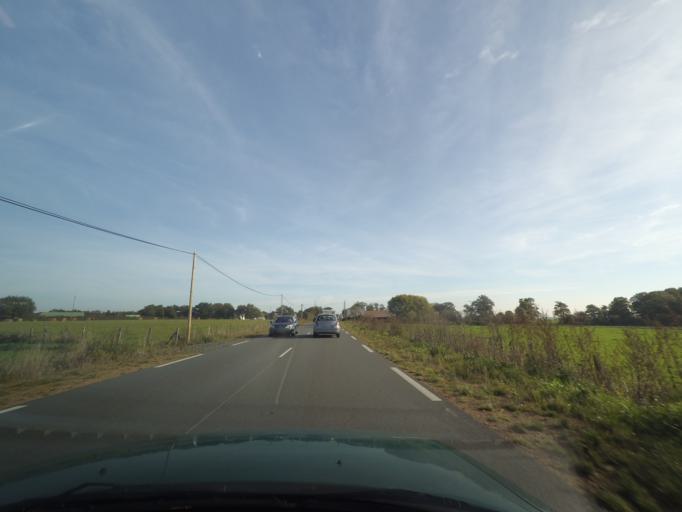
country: FR
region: Pays de la Loire
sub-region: Departement de Maine-et-Loire
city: Torfou
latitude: 47.0294
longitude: -1.0961
